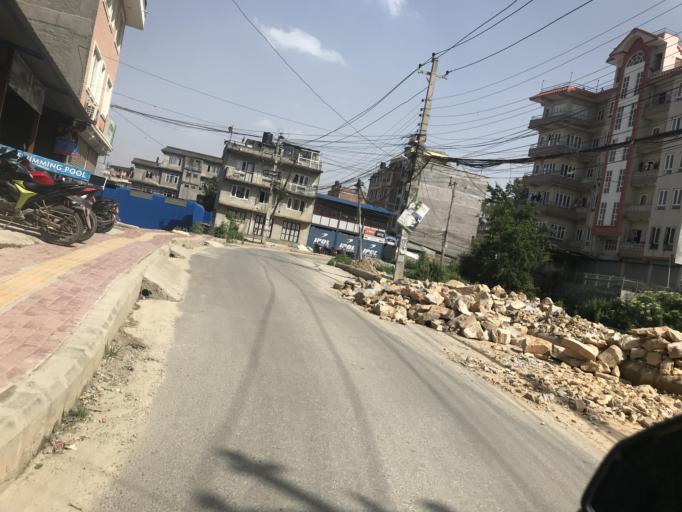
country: NP
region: Central Region
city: Kirtipur
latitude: 27.6798
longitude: 85.2785
